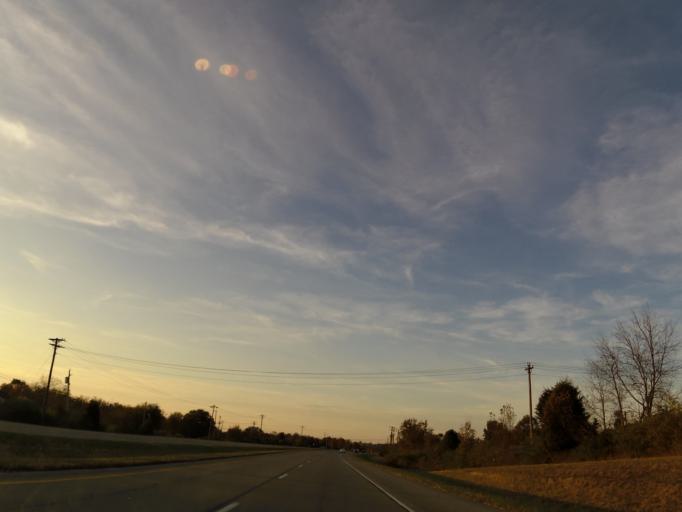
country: US
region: Kentucky
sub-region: Jessamine County
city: Nicholasville
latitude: 37.8609
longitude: -84.5922
